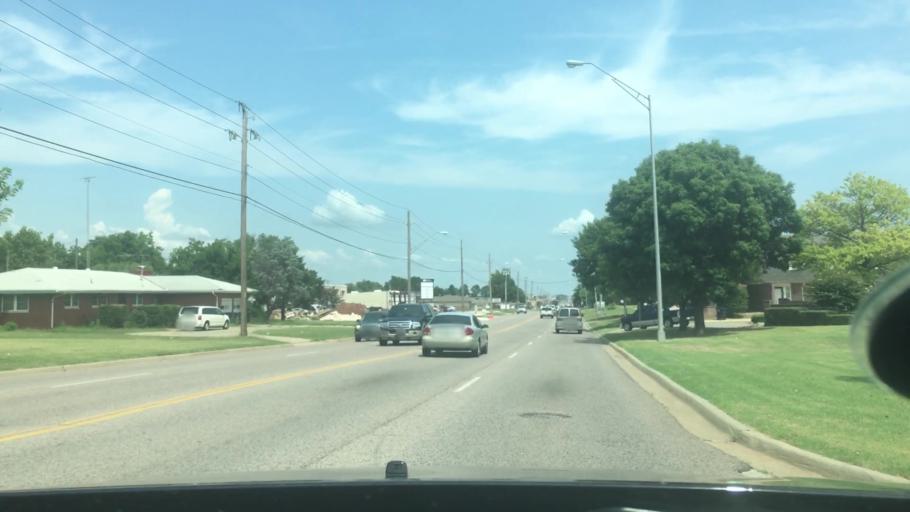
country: US
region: Oklahoma
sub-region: Pottawatomie County
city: Shawnee
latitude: 35.3691
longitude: -96.9297
